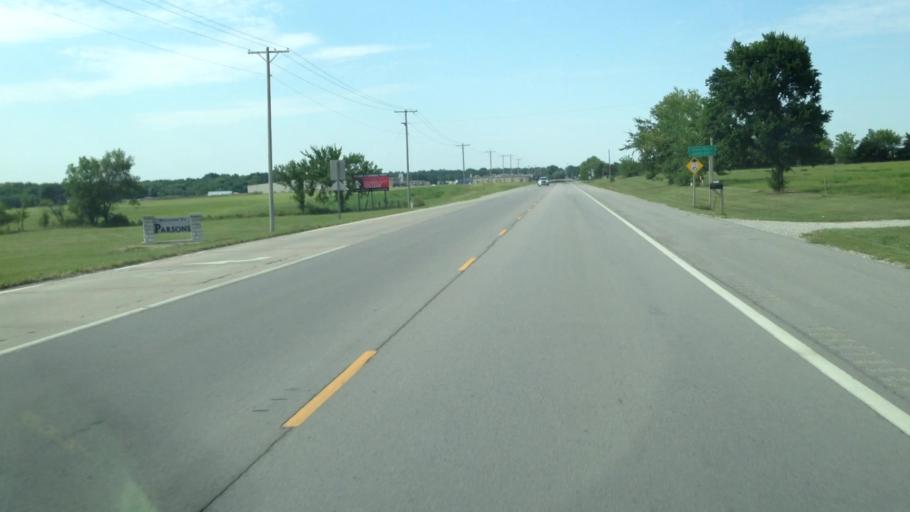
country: US
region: Kansas
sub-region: Labette County
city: Parsons
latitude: 37.3116
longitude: -95.2675
